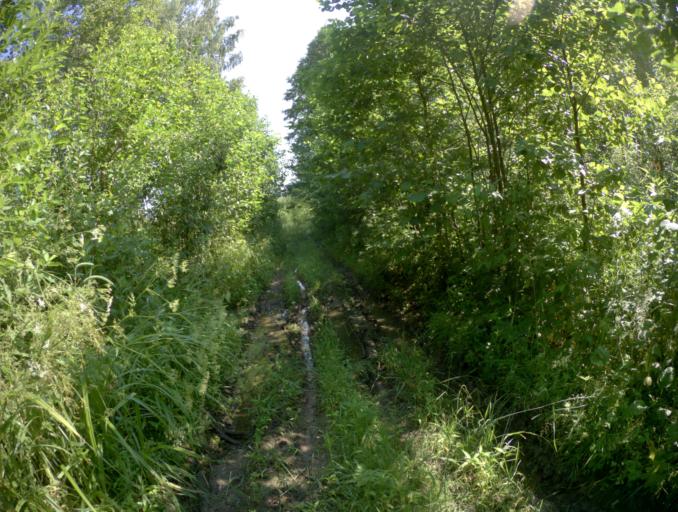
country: RU
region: Vladimir
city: Vyazniki
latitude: 56.3457
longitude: 42.1852
